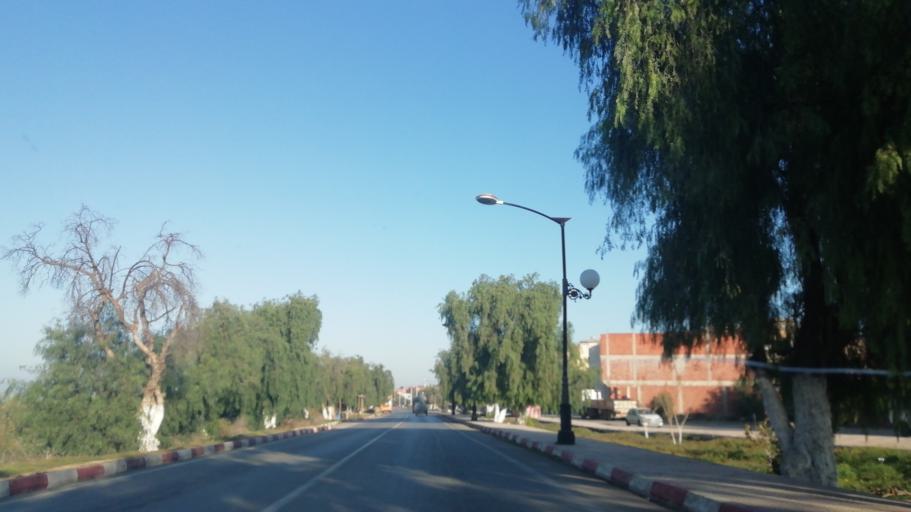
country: MA
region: Oriental
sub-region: Berkane-Taourirt
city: Ahfir
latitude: 34.9744
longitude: -2.1025
